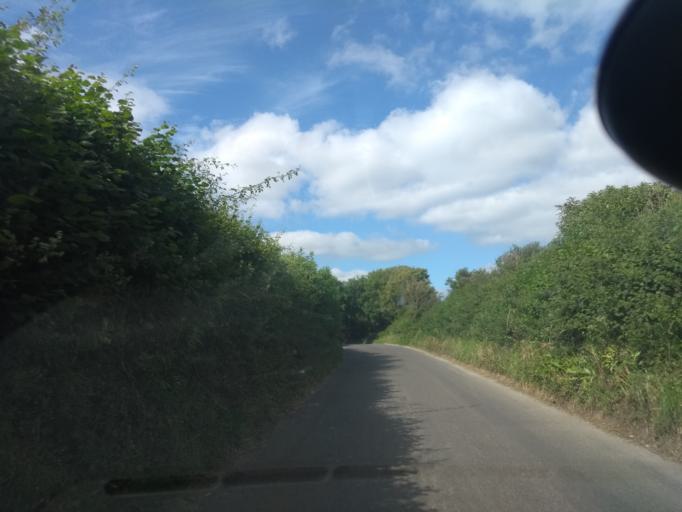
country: GB
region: England
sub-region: Devon
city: Modbury
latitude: 50.3036
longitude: -3.8865
